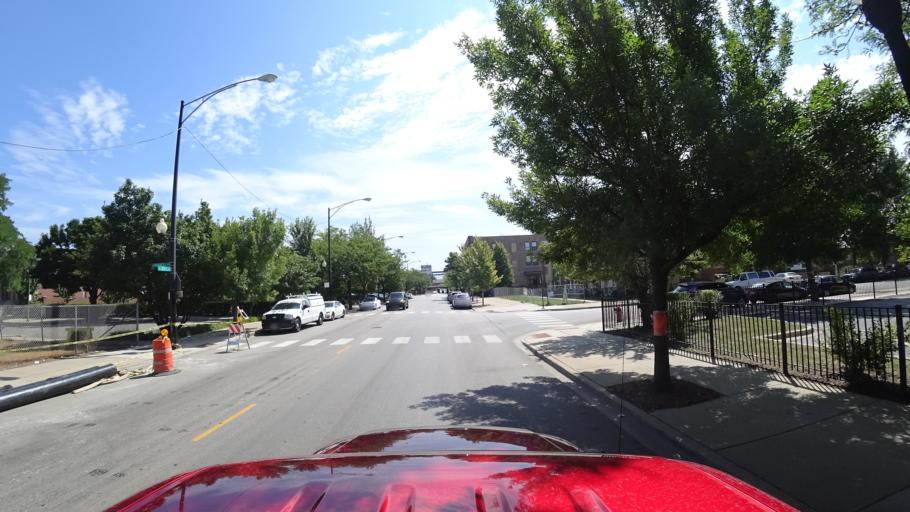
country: US
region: Illinois
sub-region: Cook County
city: Chicago
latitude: 41.8308
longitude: -87.6404
